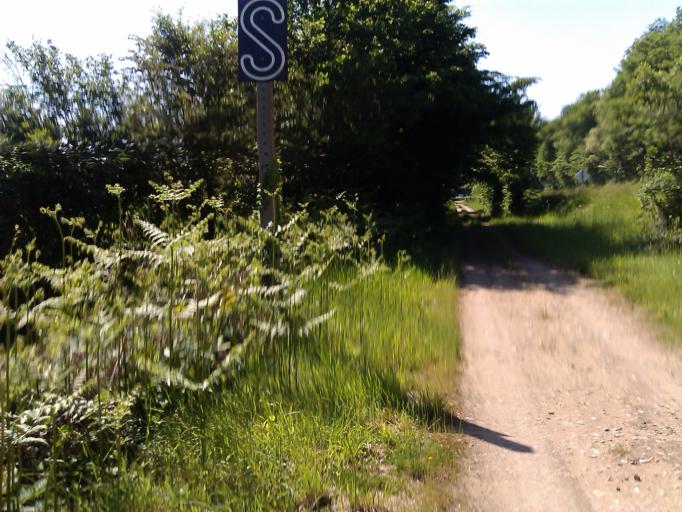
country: FR
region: Centre
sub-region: Departement de l'Indre
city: Saint-Gaultier
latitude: 46.6440
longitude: 1.3290
